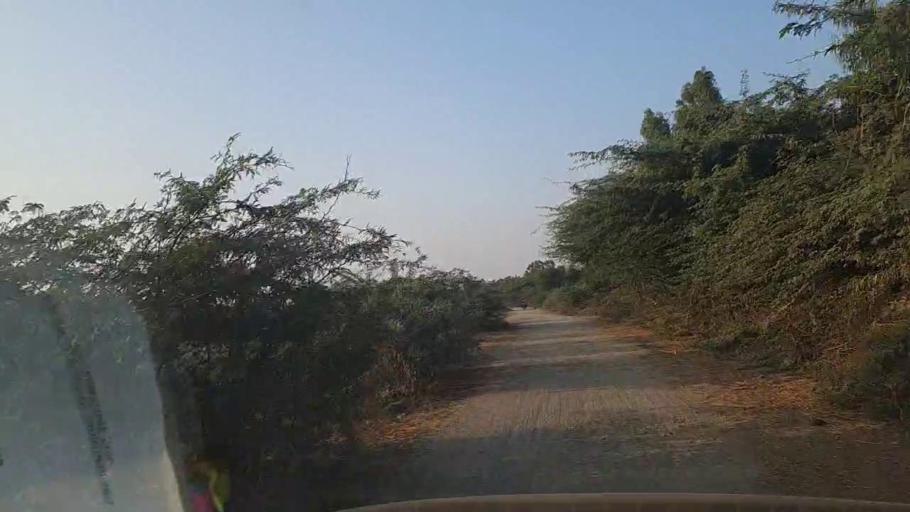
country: PK
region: Sindh
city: Keti Bandar
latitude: 24.3127
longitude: 67.6002
